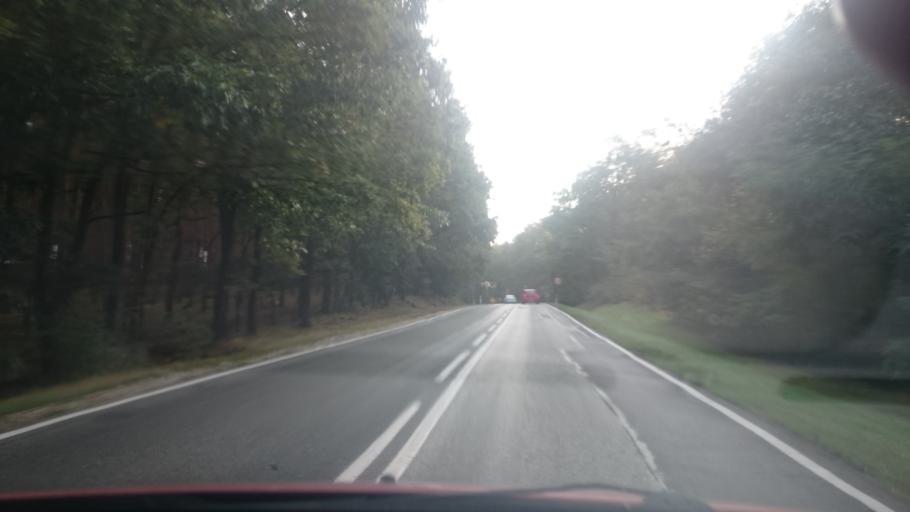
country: PL
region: Lower Silesian Voivodeship
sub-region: Powiat trzebnicki
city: Trzebnica
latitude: 51.3679
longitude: 17.1531
